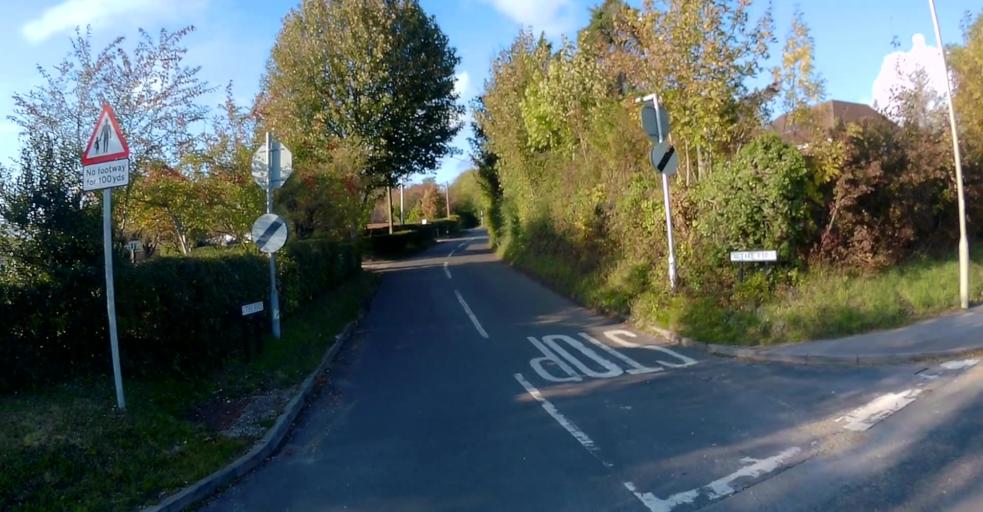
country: GB
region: England
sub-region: Hampshire
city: Odiham
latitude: 51.2451
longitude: -0.9488
